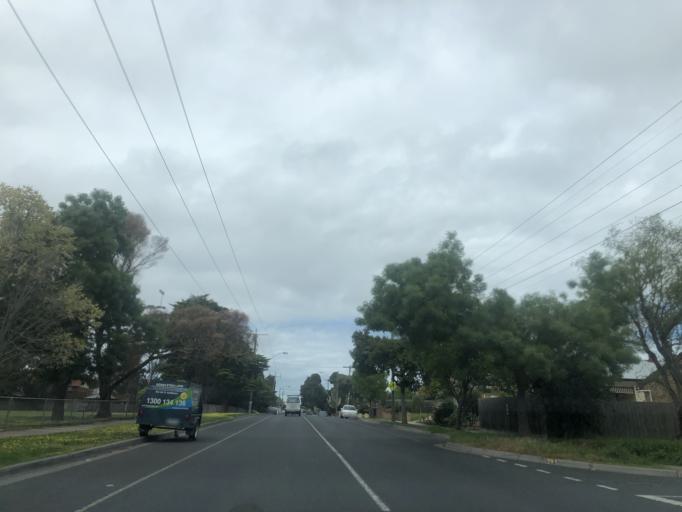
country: AU
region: Victoria
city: Murrumbeena
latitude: -37.9053
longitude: 145.0748
